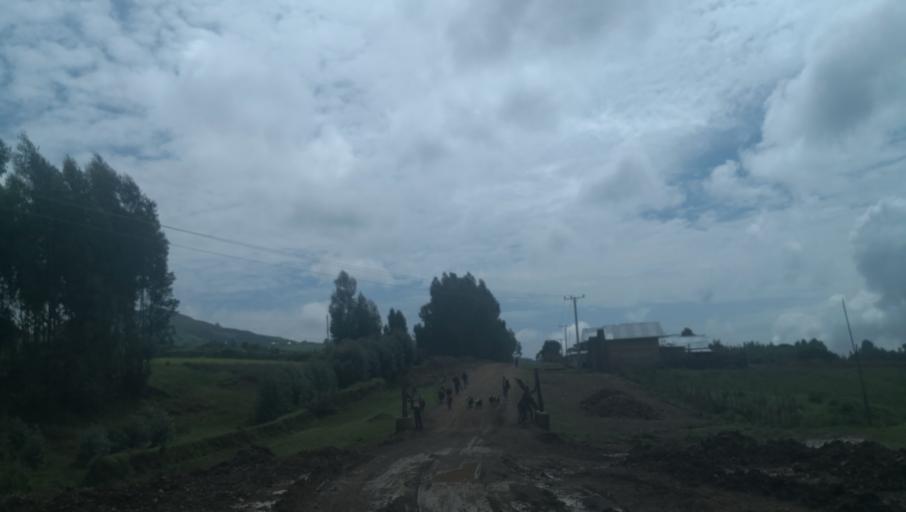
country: ET
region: Southern Nations, Nationalities, and People's Region
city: Butajira
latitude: 8.3316
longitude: 38.4079
